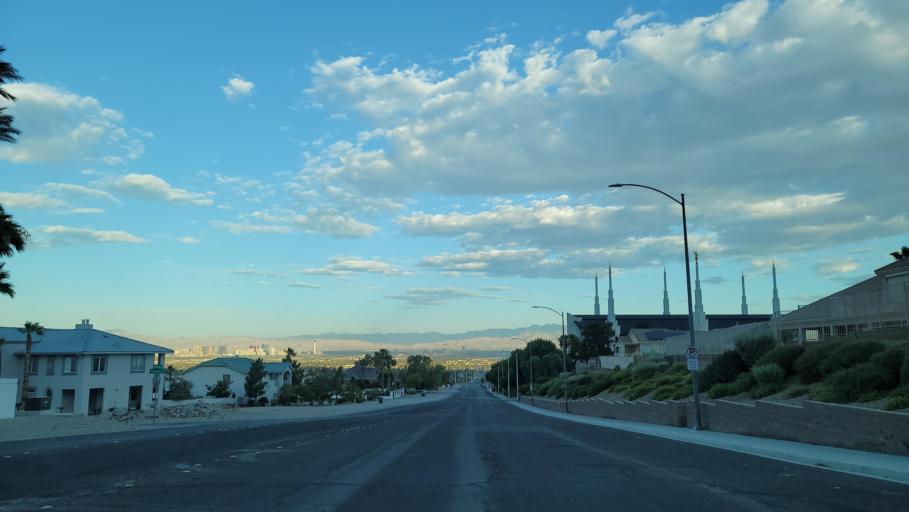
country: US
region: Nevada
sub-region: Clark County
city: Sunrise Manor
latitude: 36.1740
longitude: -115.0173
